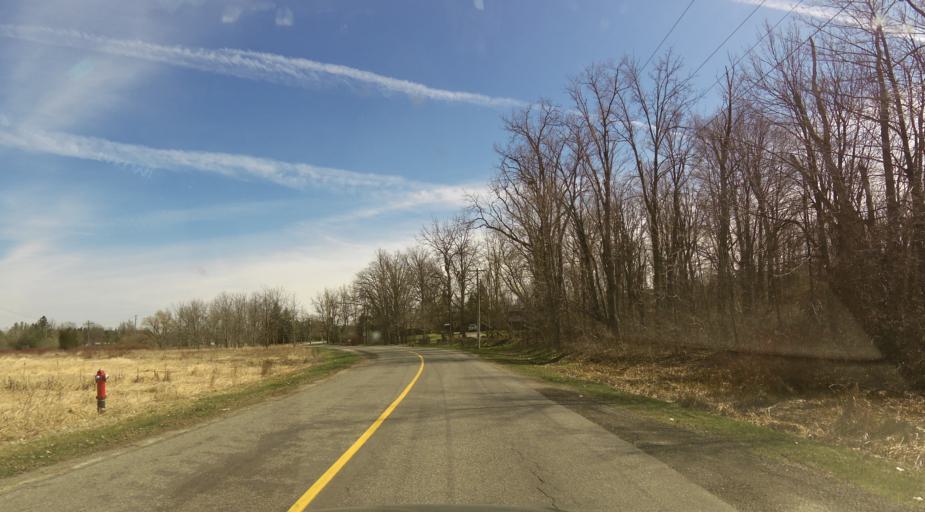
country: CA
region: Ontario
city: Brampton
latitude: 43.6342
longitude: -79.7660
